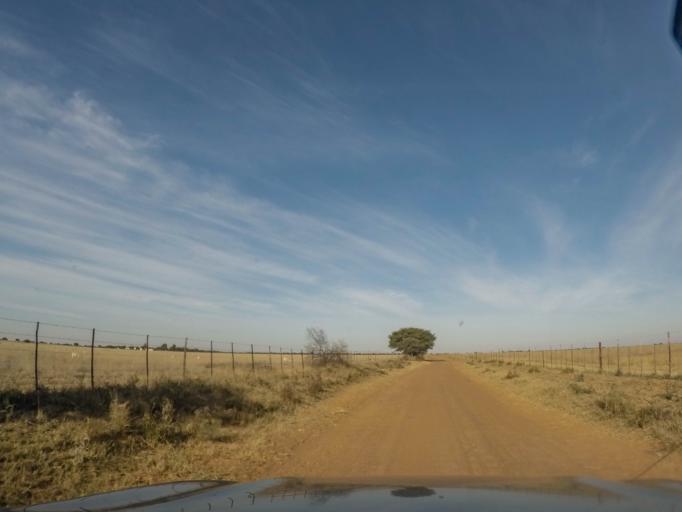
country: BW
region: South East
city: Janeng
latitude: -25.6435
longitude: 25.2591
